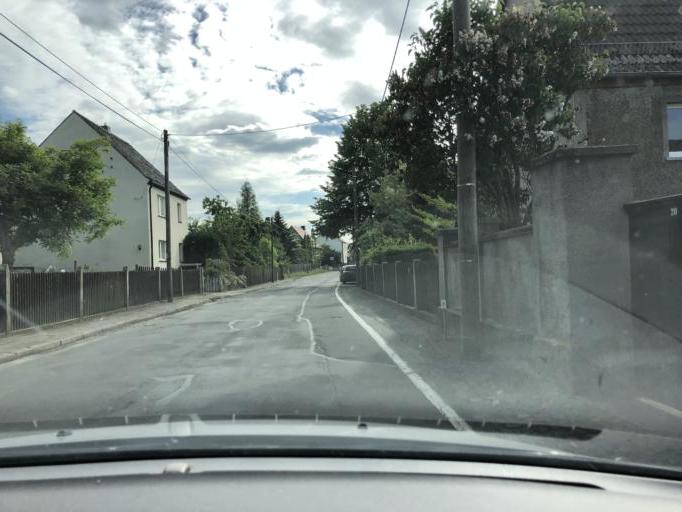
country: DE
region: Saxony
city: Trebsen
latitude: 51.2763
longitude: 12.7218
